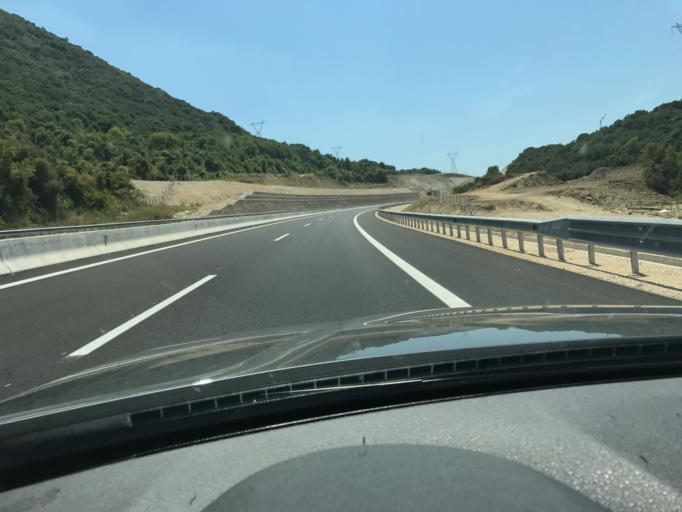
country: GR
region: Epirus
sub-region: Nomos Ioanninon
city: Agia Kyriaki
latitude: 39.5046
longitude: 20.8901
